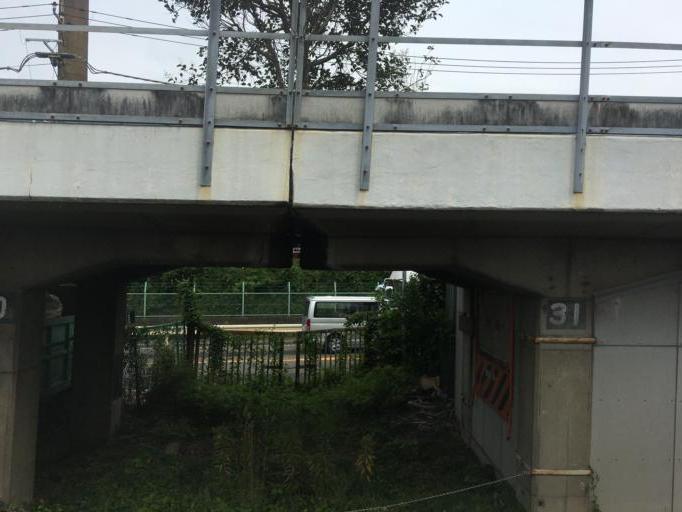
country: JP
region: Kanagawa
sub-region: Kawasaki-shi
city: Kawasaki
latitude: 35.5058
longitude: 139.7100
